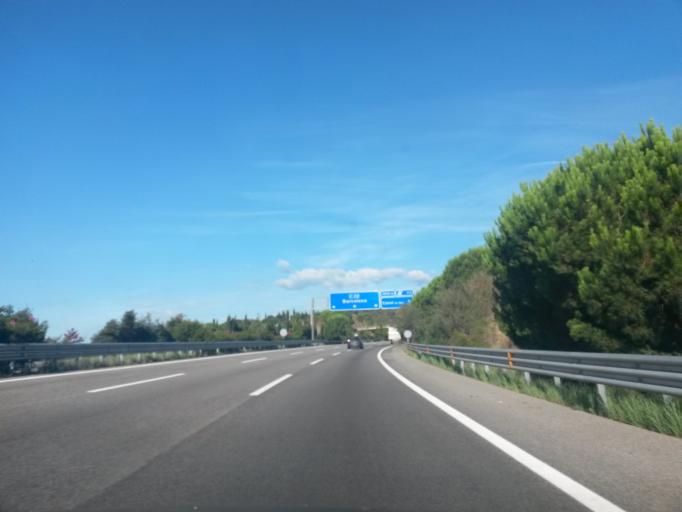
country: ES
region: Catalonia
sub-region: Provincia de Barcelona
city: Canet de Mar
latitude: 41.5998
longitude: 2.5862
